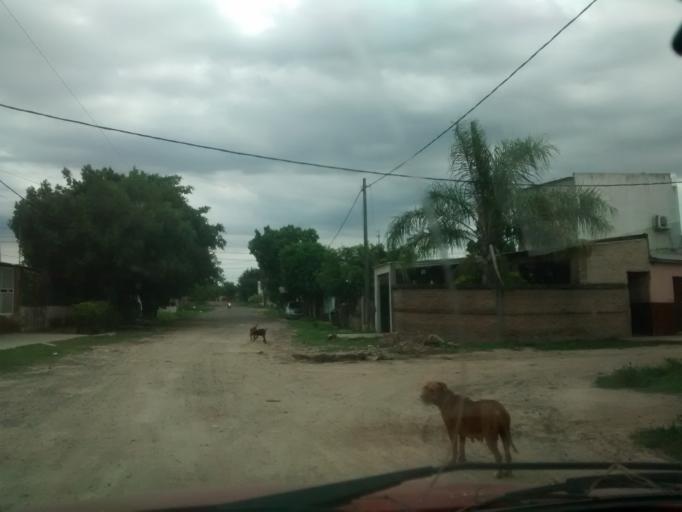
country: AR
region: Chaco
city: Resistencia
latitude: -27.4244
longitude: -58.9743
